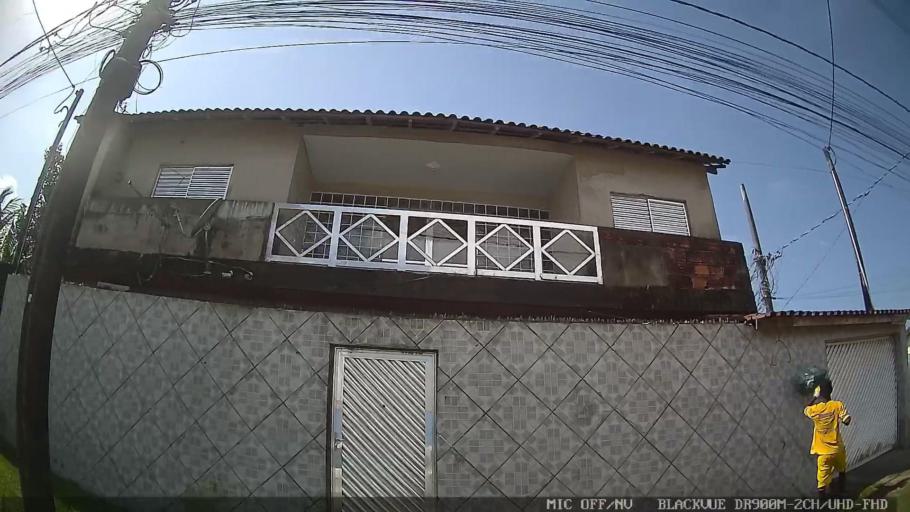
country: BR
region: Sao Paulo
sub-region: Guaruja
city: Guaruja
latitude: -23.9751
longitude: -46.2001
